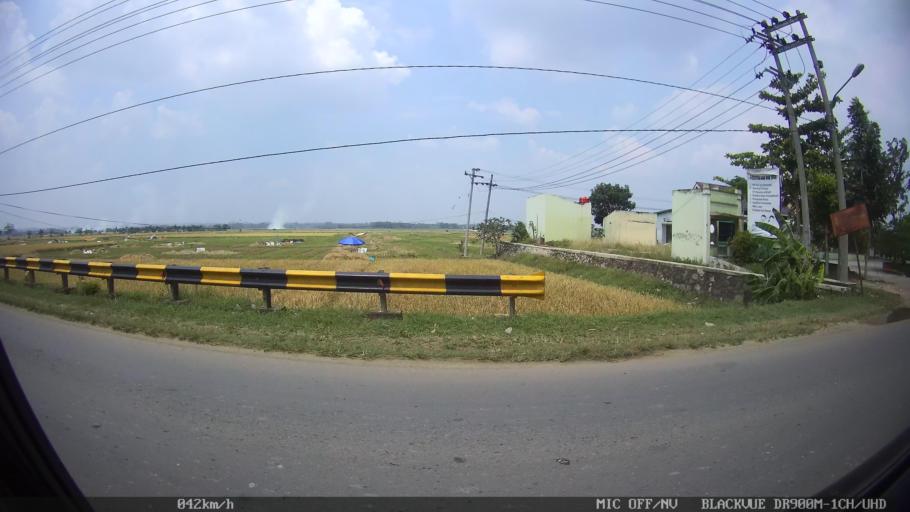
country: ID
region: Lampung
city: Pringsewu
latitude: -5.3721
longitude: 105.0121
